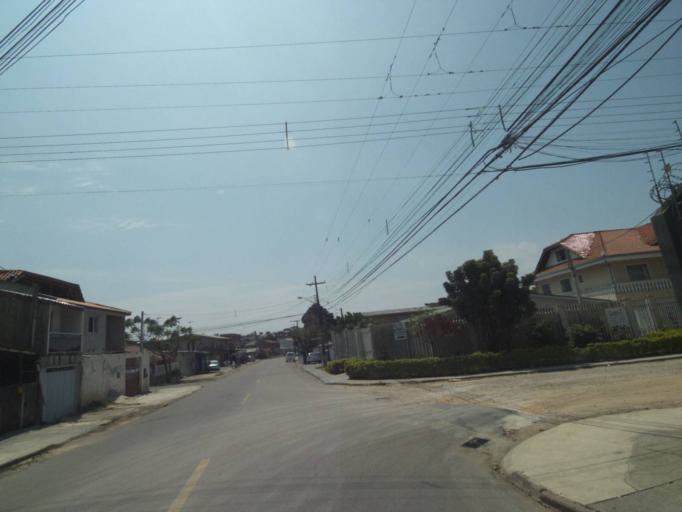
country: BR
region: Parana
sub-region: Curitiba
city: Curitiba
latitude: -25.4851
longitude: -49.3160
